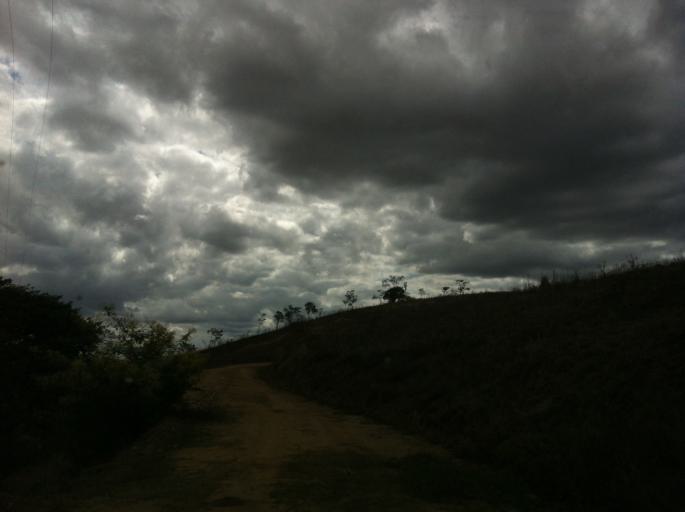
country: BR
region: Alagoas
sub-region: Ibateguara
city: Ibateguara
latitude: -8.9617
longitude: -35.9505
